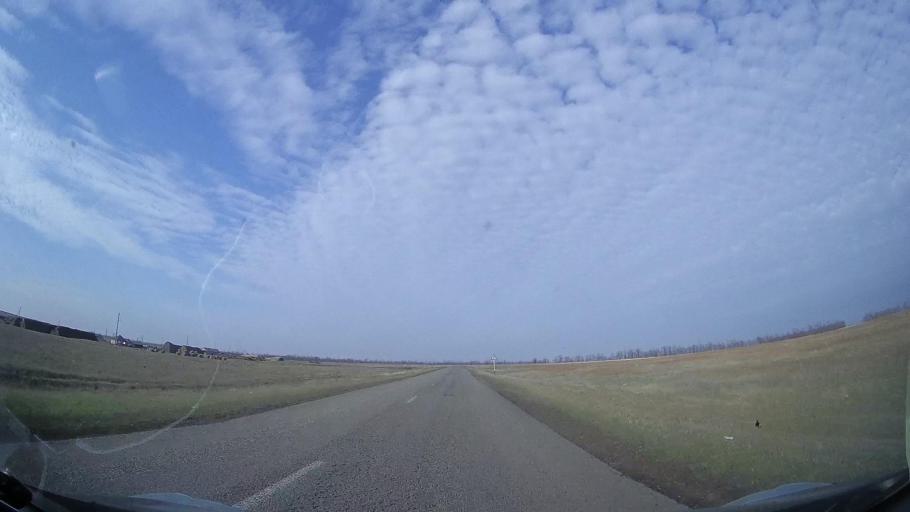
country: RU
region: Rostov
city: Gigant
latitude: 46.8474
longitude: 41.3254
